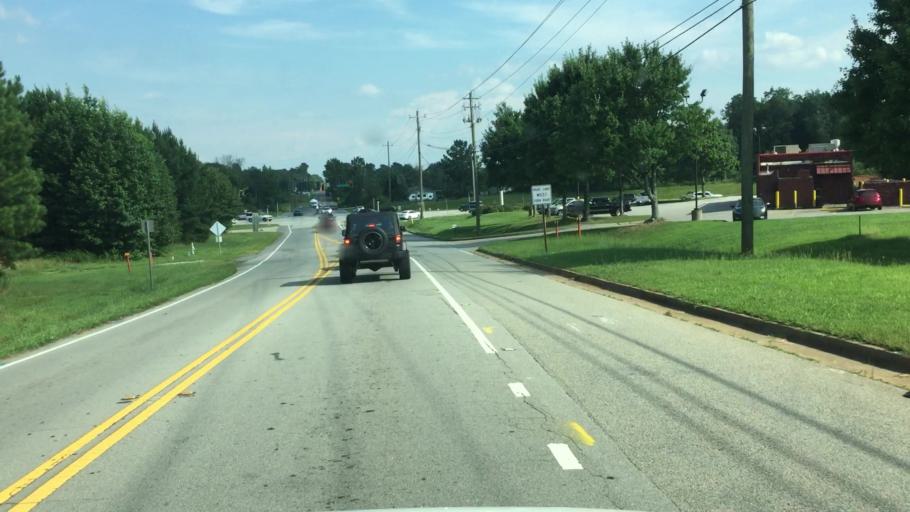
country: US
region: Georgia
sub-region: Gwinnett County
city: Dacula
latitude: 33.9751
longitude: -83.8925
